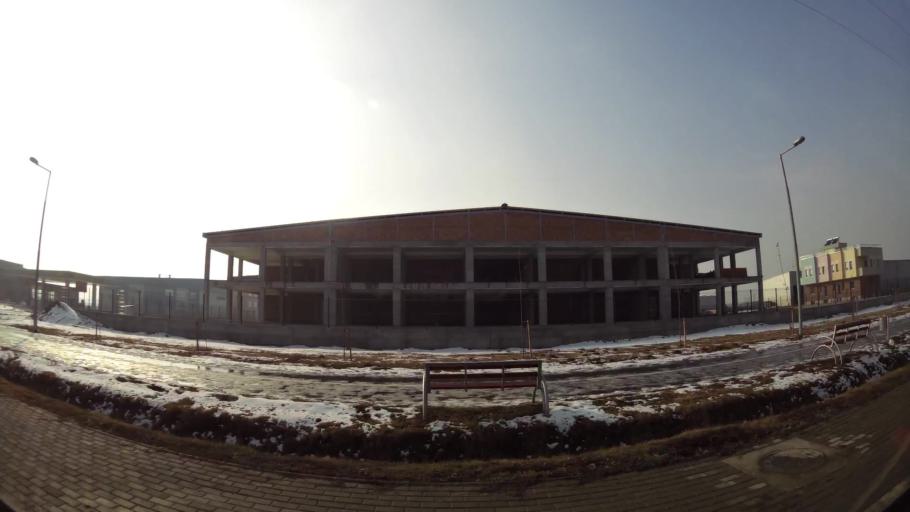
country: MK
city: Kadino
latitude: 41.9789
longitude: 21.5932
